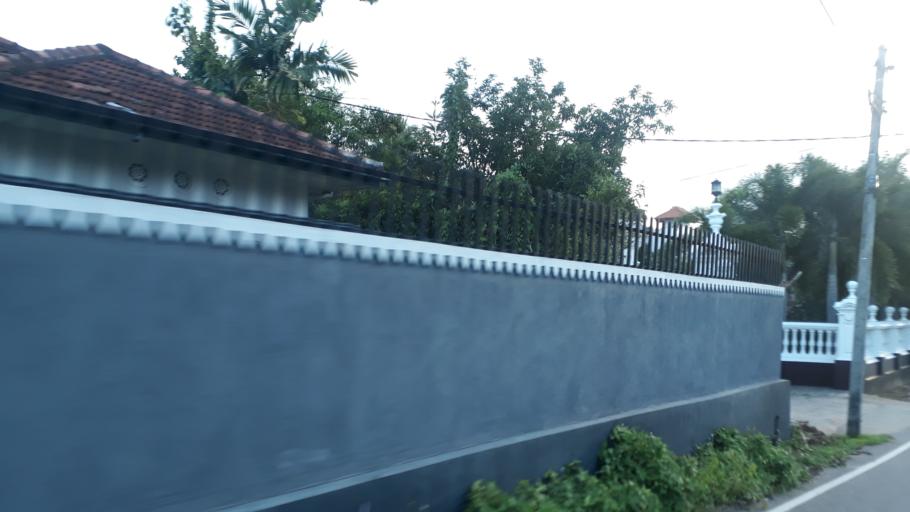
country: LK
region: Western
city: Gampaha
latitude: 7.1022
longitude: 79.9884
